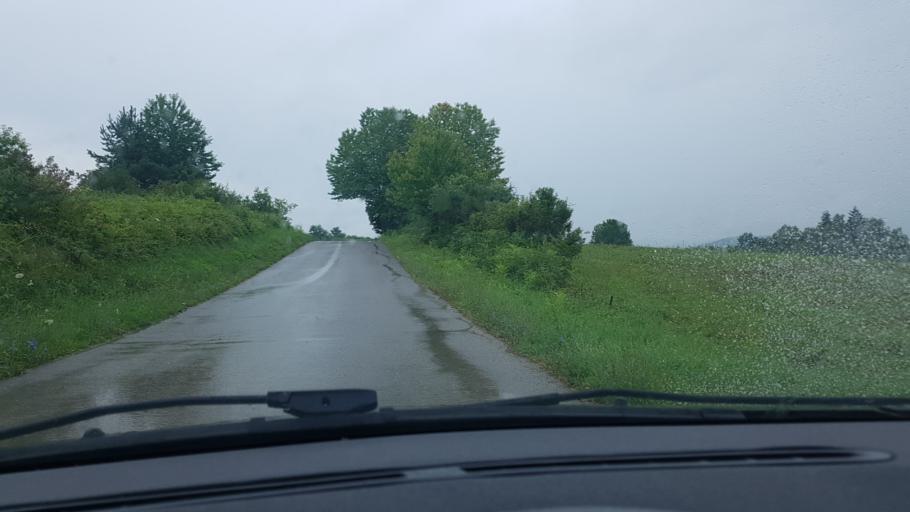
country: HR
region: Licko-Senjska
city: Jezerce
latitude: 44.9900
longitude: 15.6627
